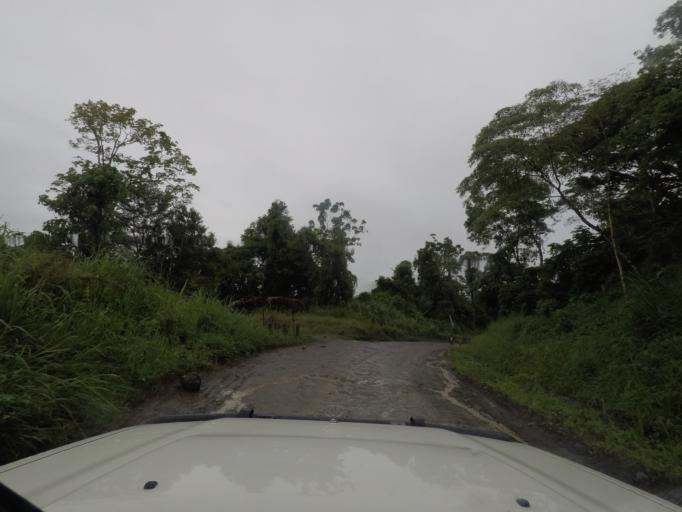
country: PG
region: Madang
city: Madang
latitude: -5.4558
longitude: 145.5060
